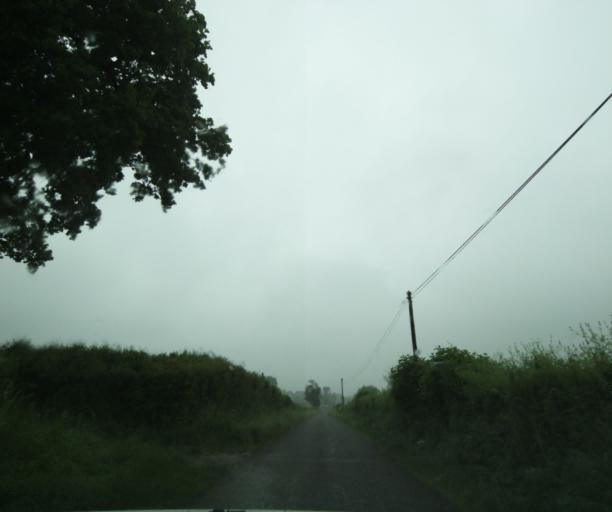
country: FR
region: Bourgogne
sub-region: Departement de Saone-et-Loire
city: Charolles
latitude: 46.4034
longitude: 4.2943
